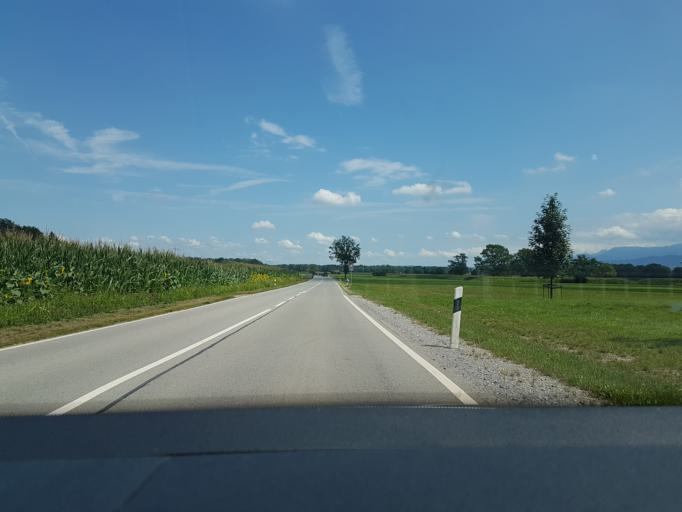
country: DE
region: Bavaria
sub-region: Upper Bavaria
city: Bad Feilnbach
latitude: 47.8005
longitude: 11.9922
